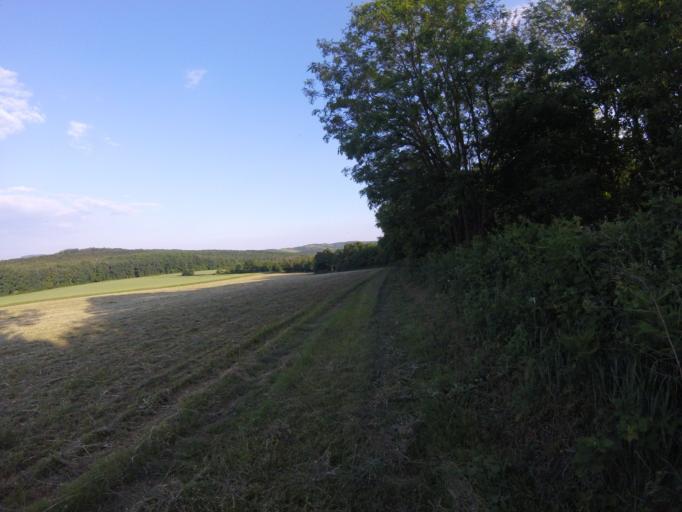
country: HU
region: Zala
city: Zalaszentgrot
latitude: 46.8803
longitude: 17.1335
